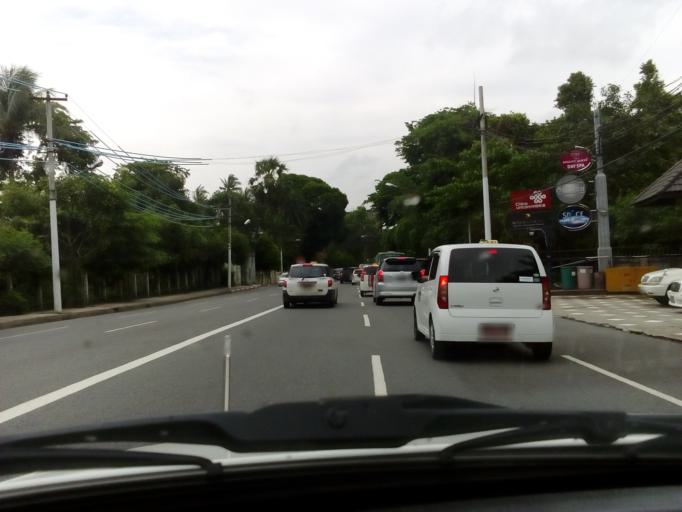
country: MM
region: Yangon
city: Yangon
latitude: 16.8216
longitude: 96.1547
